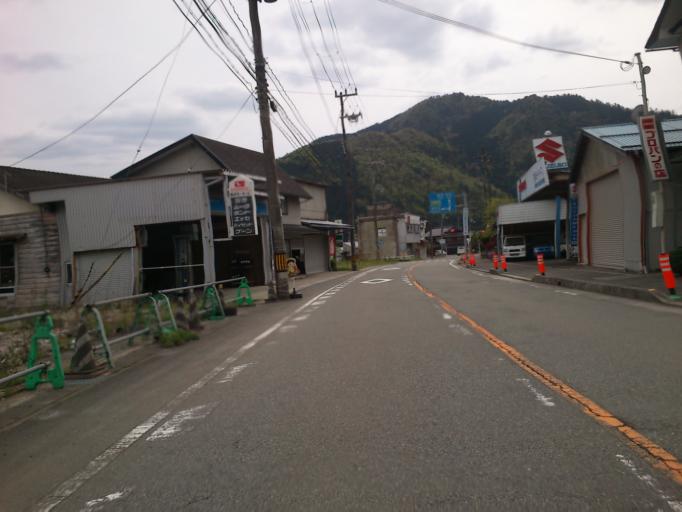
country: JP
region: Kyoto
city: Maizuru
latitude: 35.2749
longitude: 135.5457
